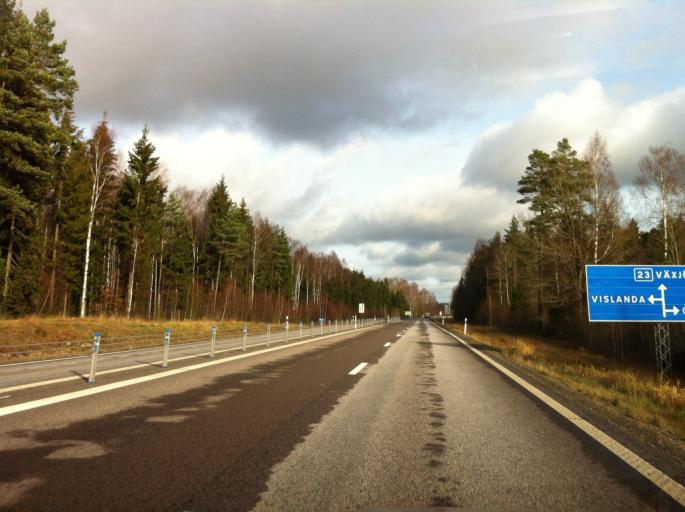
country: SE
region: Kronoberg
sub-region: Alvesta Kommun
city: Vislanda
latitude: 56.7206
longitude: 14.4599
